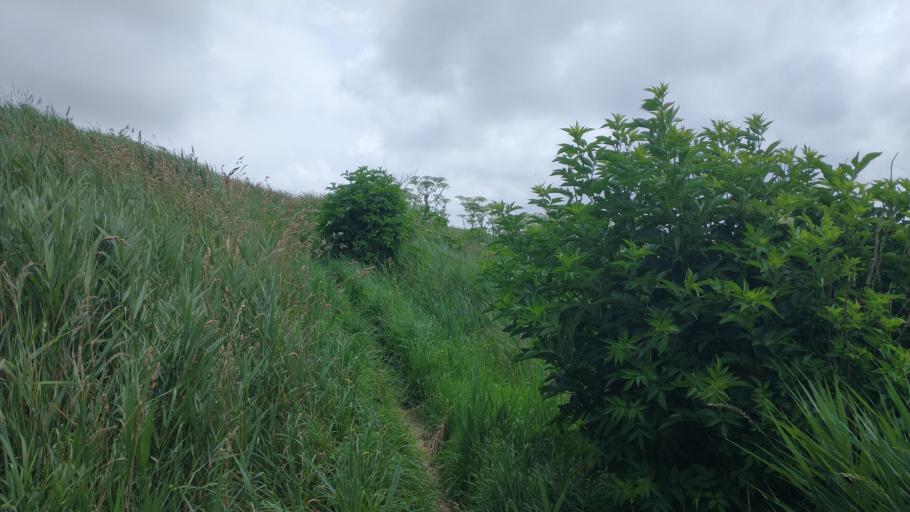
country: NL
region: North Holland
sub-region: Gemeente Den Helder
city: Den Helder
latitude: 53.0077
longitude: 4.7647
